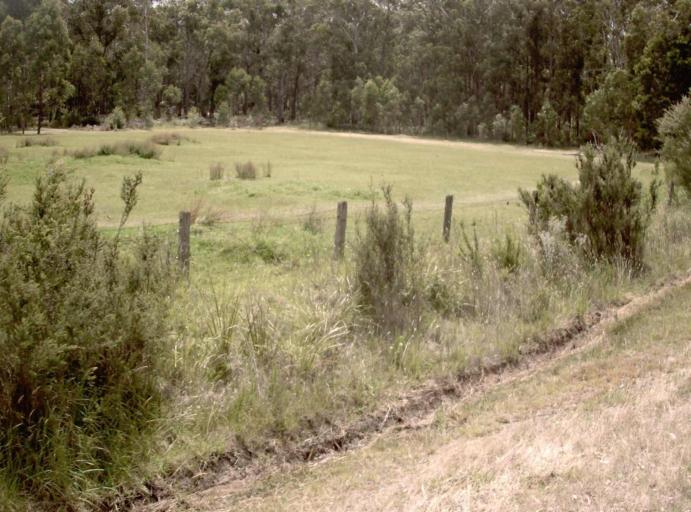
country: AU
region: Victoria
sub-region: Latrobe
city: Traralgon
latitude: -38.5059
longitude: 146.6500
